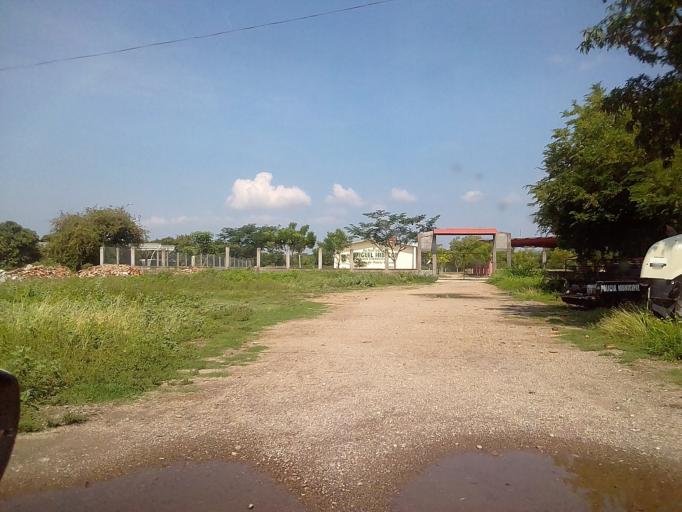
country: MX
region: Oaxaca
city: San Francisco Ixhuatan
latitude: 16.3932
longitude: -94.4584
